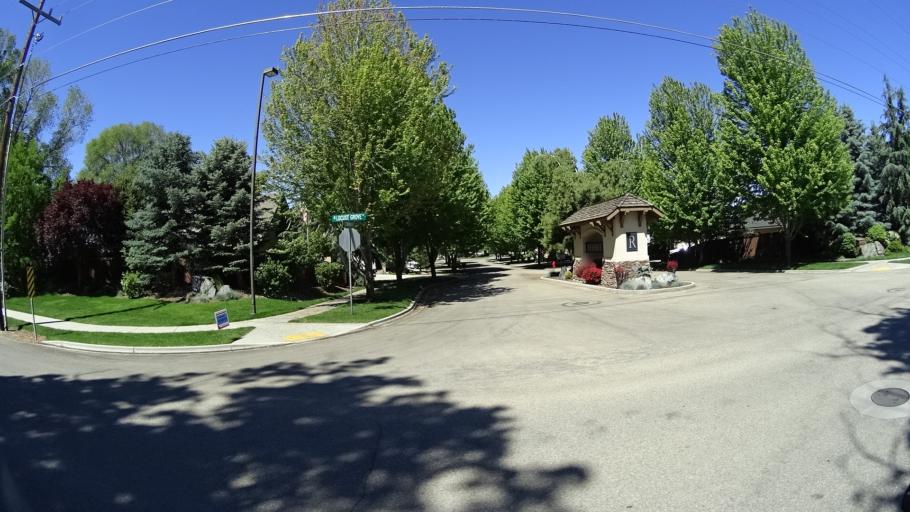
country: US
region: Idaho
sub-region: Ada County
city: Eagle
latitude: 43.6587
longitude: -116.3745
